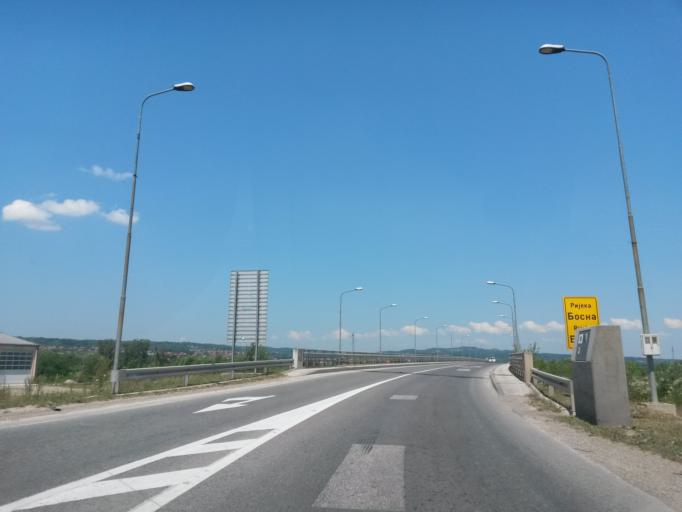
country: BA
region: Federation of Bosnia and Herzegovina
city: Odzak
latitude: 44.9688
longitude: 18.2996
